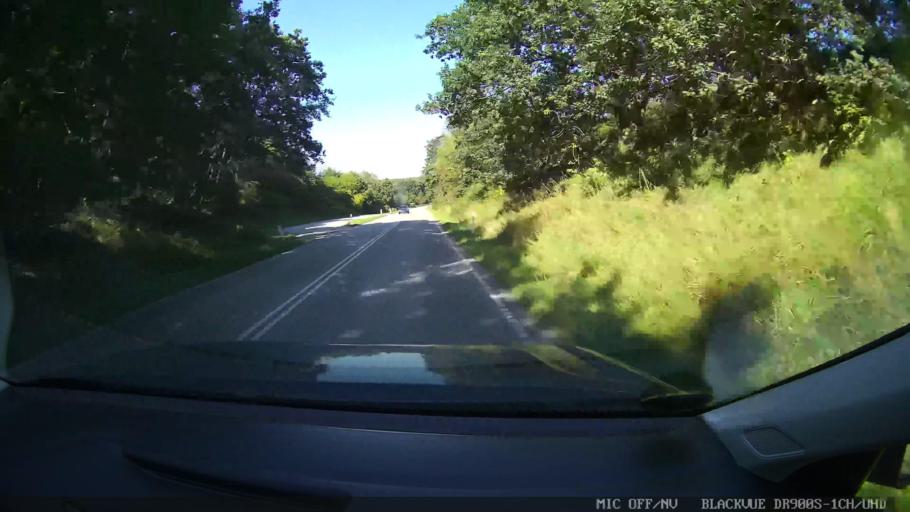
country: DK
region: North Denmark
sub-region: Mariagerfjord Kommune
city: Mariager
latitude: 56.5974
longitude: 9.9987
